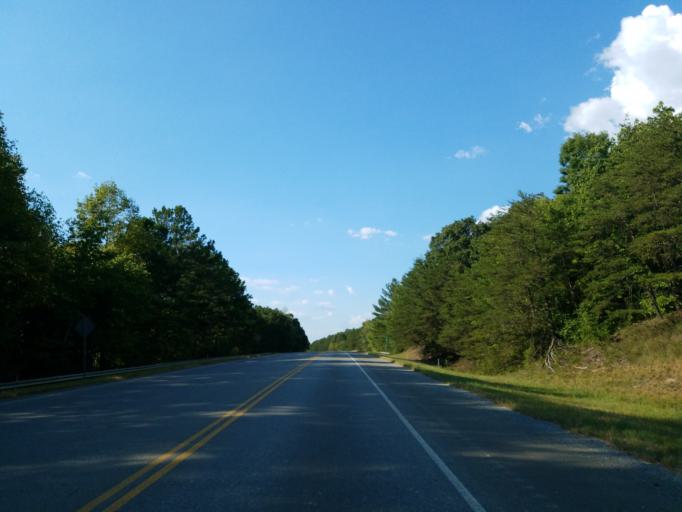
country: US
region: Georgia
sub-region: Murray County
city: Chatsworth
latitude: 34.6822
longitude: -84.7285
